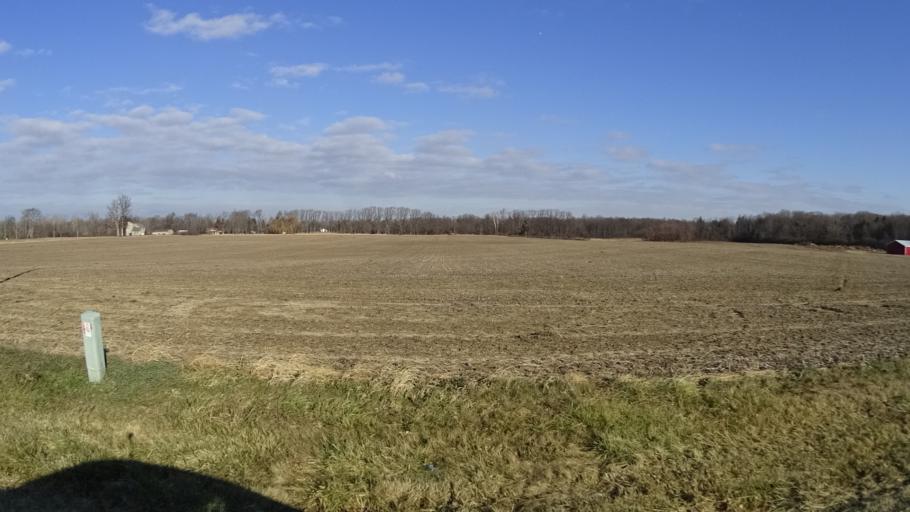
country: US
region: Ohio
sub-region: Lorain County
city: Oberlin
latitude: 41.2510
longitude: -82.2050
